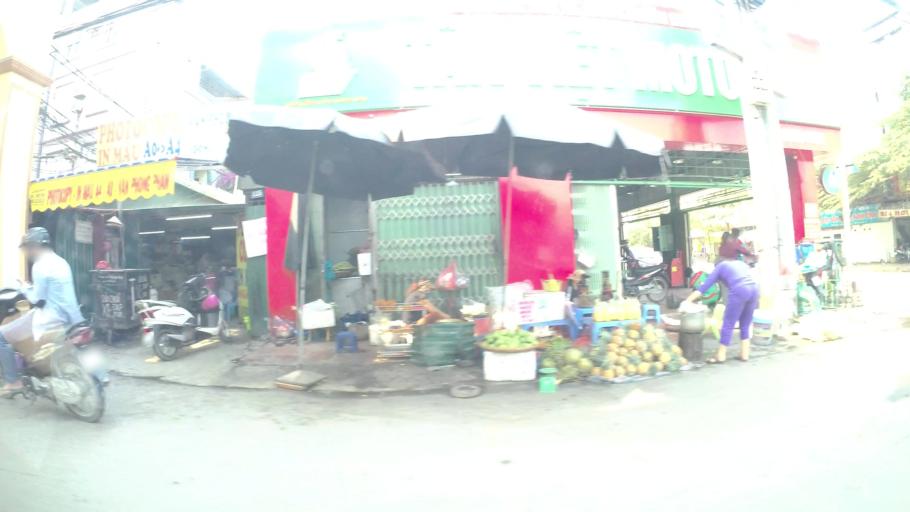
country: VN
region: Ha Noi
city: Van Dien
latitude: 20.9716
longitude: 105.8358
